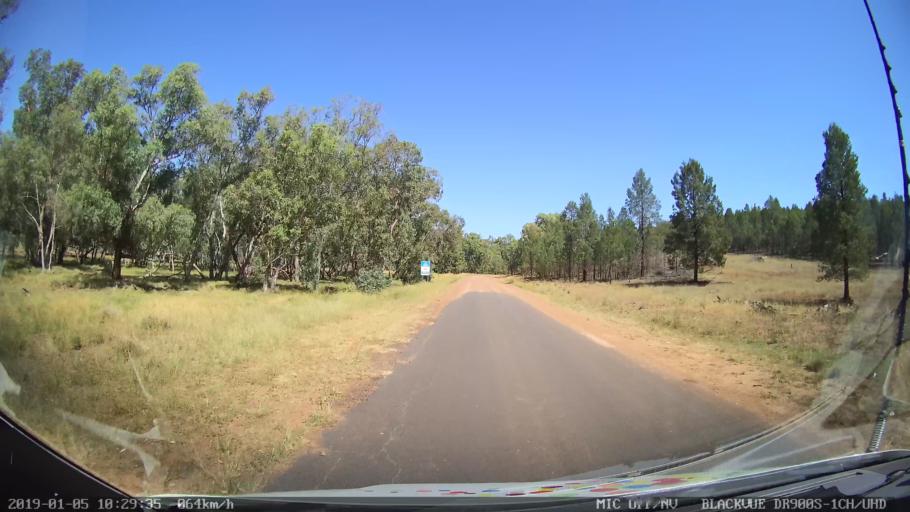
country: AU
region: New South Wales
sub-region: Gilgandra
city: Gilgandra
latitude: -31.5391
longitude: 148.9286
